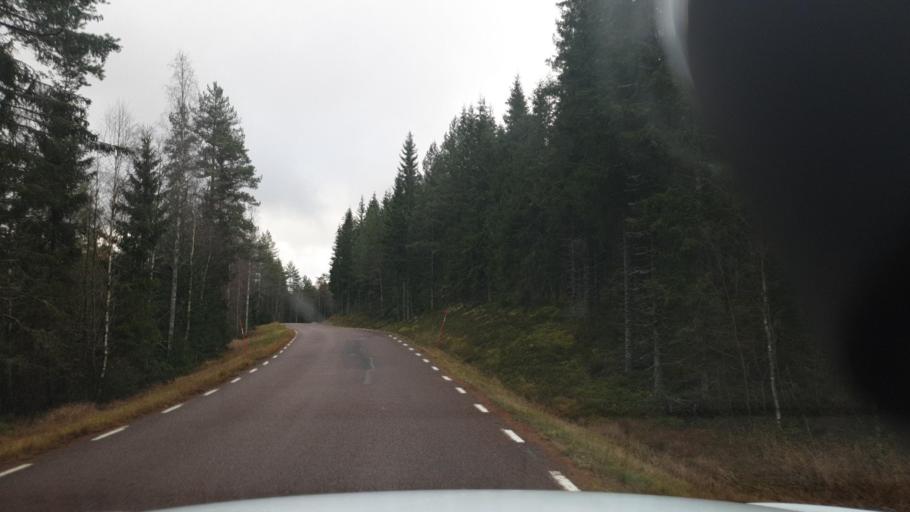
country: SE
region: Vaermland
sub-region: Arvika Kommun
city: Arvika
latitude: 59.8079
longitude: 12.8335
